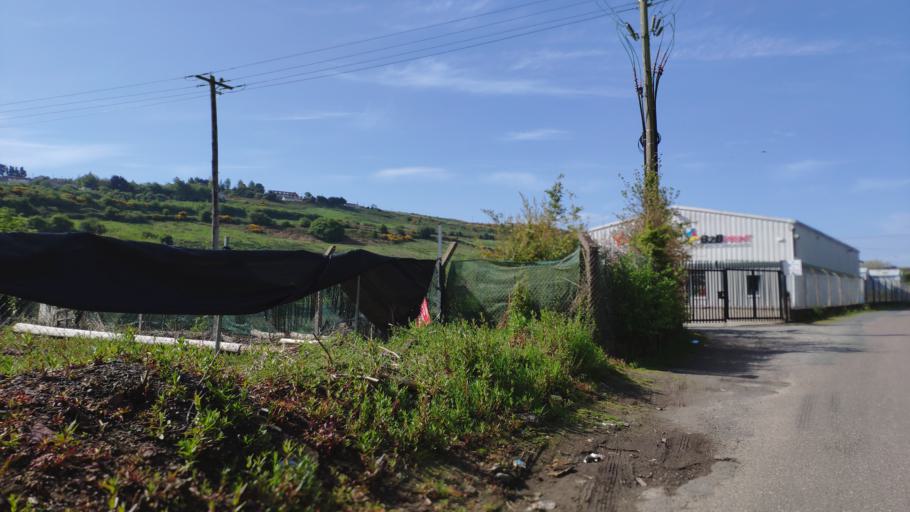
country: IE
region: Munster
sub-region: County Cork
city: Cork
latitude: 51.9205
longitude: -8.5017
